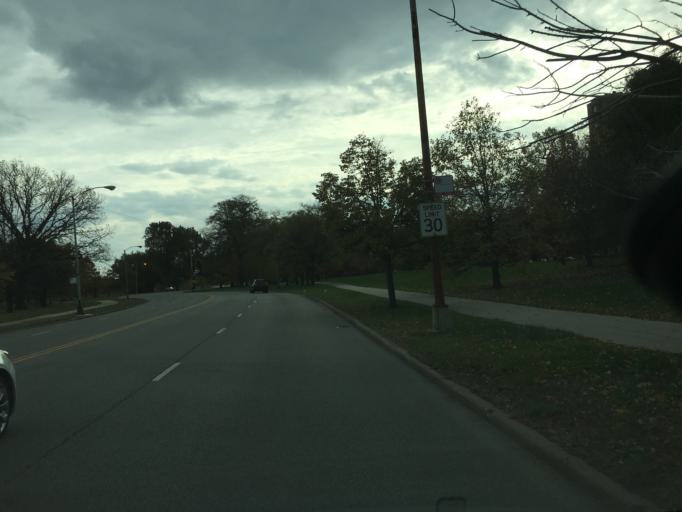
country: US
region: Illinois
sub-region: Cook County
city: Chicago
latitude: 41.7905
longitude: -87.5855
